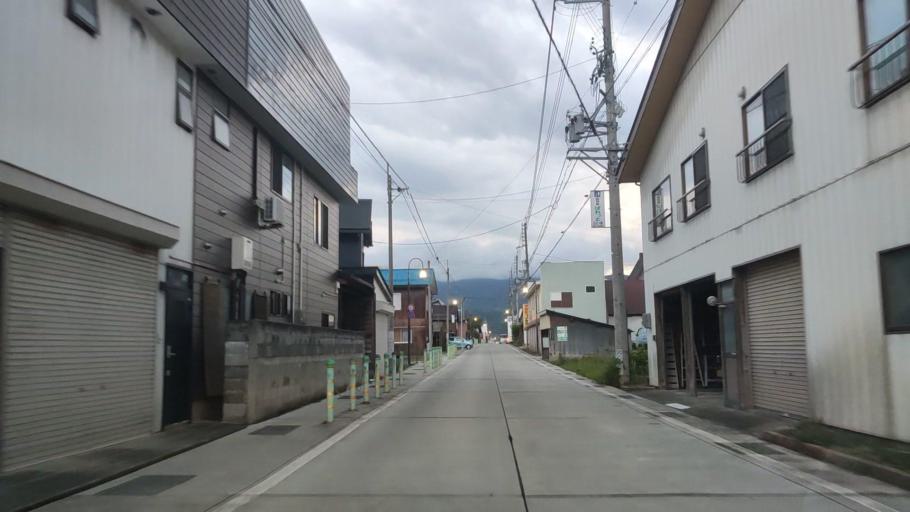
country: JP
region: Nagano
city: Iiyama
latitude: 36.8661
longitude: 138.4070
